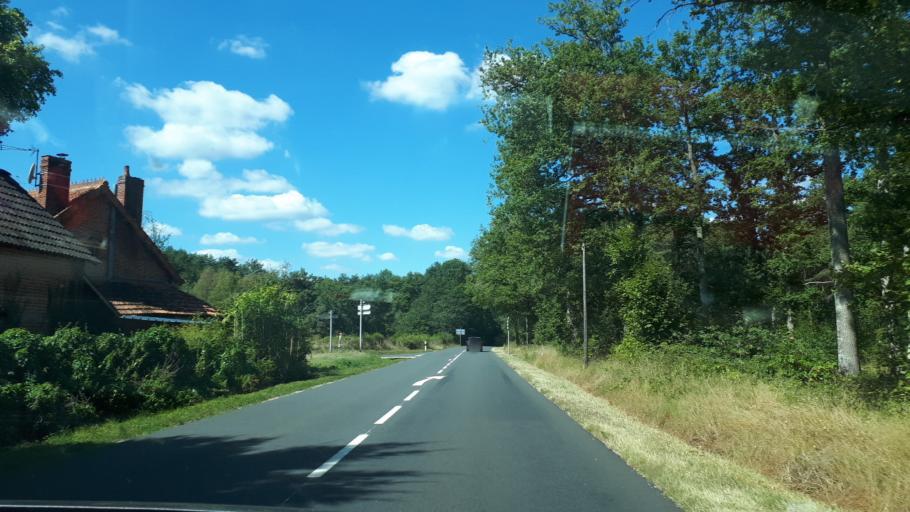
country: FR
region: Centre
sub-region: Departement du Loir-et-Cher
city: Saint-Viatre
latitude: 47.5745
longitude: 1.9648
